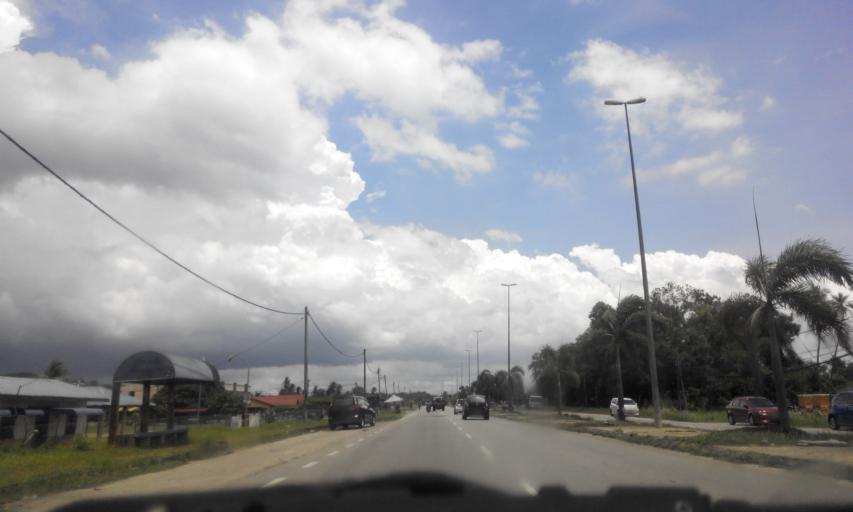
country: MY
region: Perak
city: Parit Buntar
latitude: 5.1173
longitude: 100.5250
